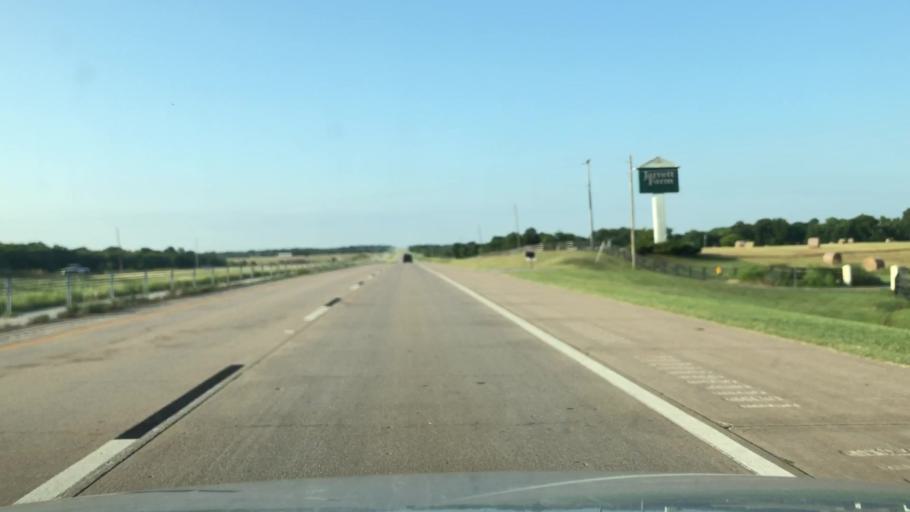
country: US
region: Oklahoma
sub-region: Osage County
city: Skiatook
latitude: 36.4595
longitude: -95.9207
